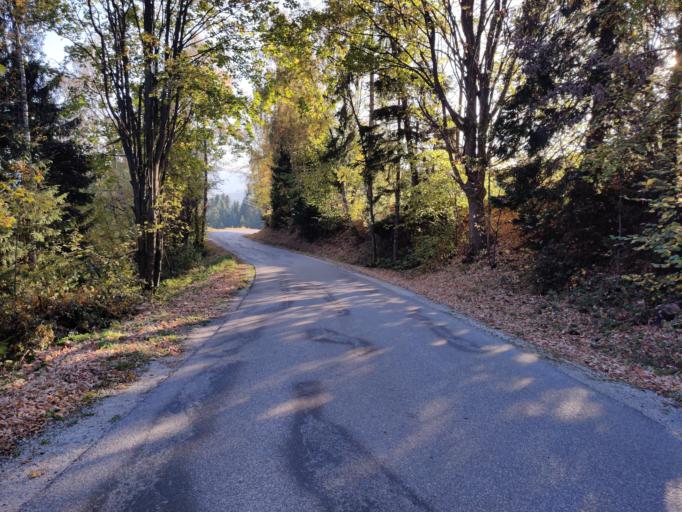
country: AT
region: Styria
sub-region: Politischer Bezirk Hartberg-Fuerstenfeld
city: Sankt Jakob im Walde
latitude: 47.4736
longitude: 15.7912
